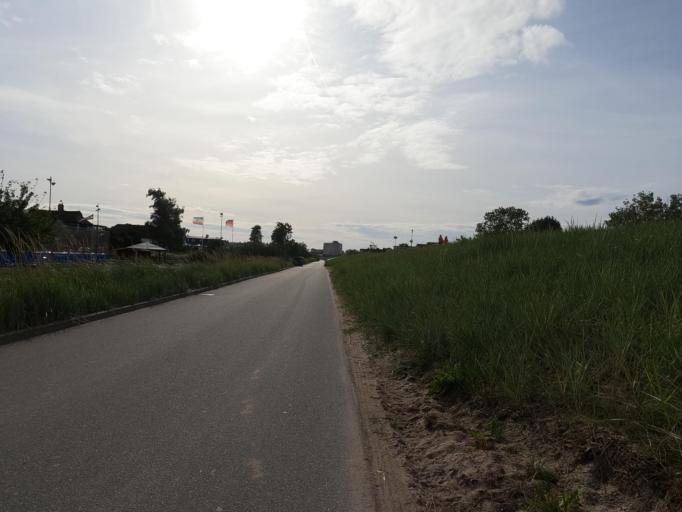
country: DE
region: Schleswig-Holstein
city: Dahme
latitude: 54.2251
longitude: 11.0869
